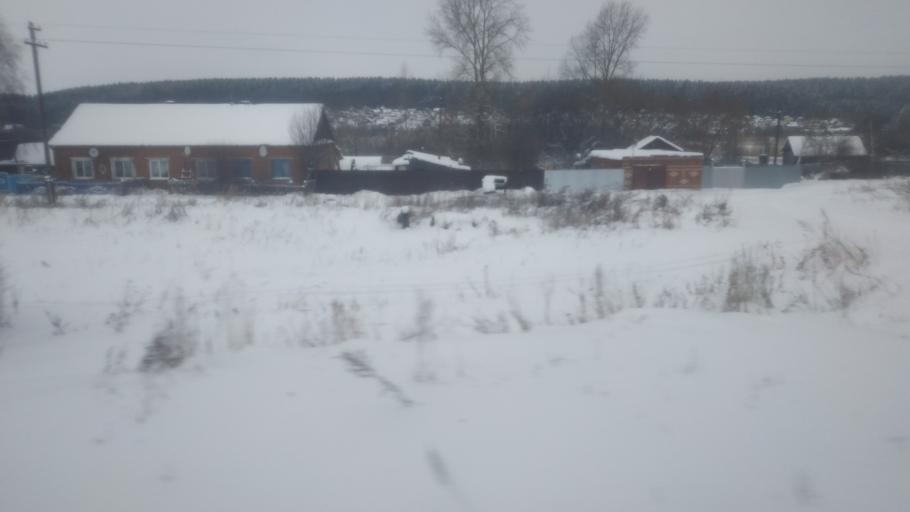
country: RU
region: Udmurtiya
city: Sigayevo
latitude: 56.4536
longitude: 53.6864
